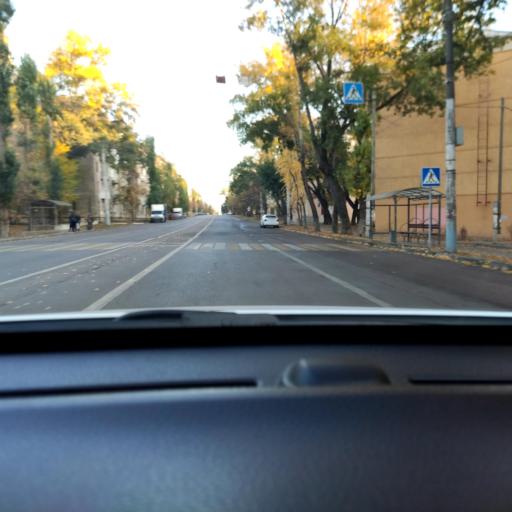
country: RU
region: Voronezj
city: Maslovka
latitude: 51.6224
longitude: 39.2391
